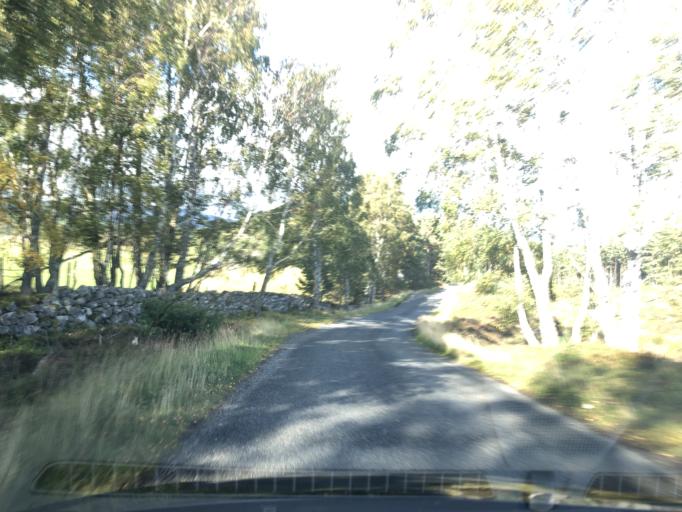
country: GB
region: Scotland
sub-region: Highland
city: Aviemore
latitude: 57.0826
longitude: -3.9000
